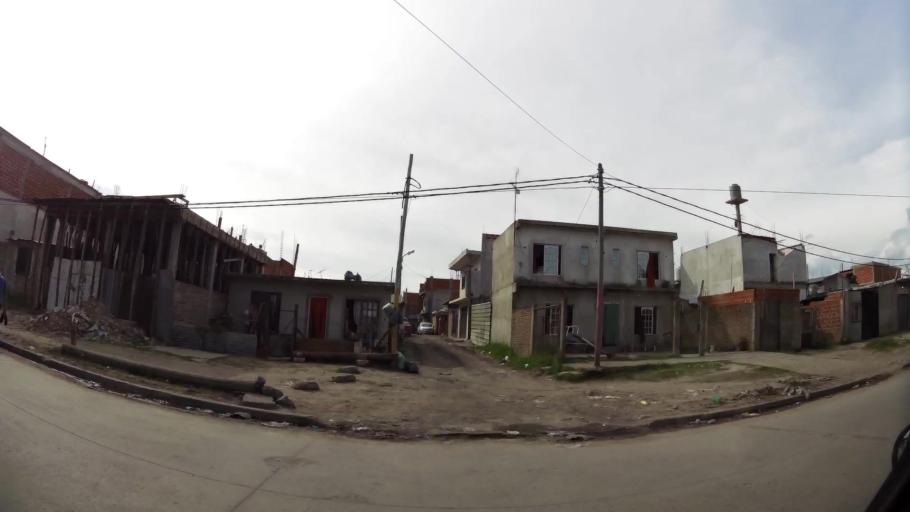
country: AR
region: Buenos Aires
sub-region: Partido de Quilmes
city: Quilmes
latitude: -34.7595
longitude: -58.2548
